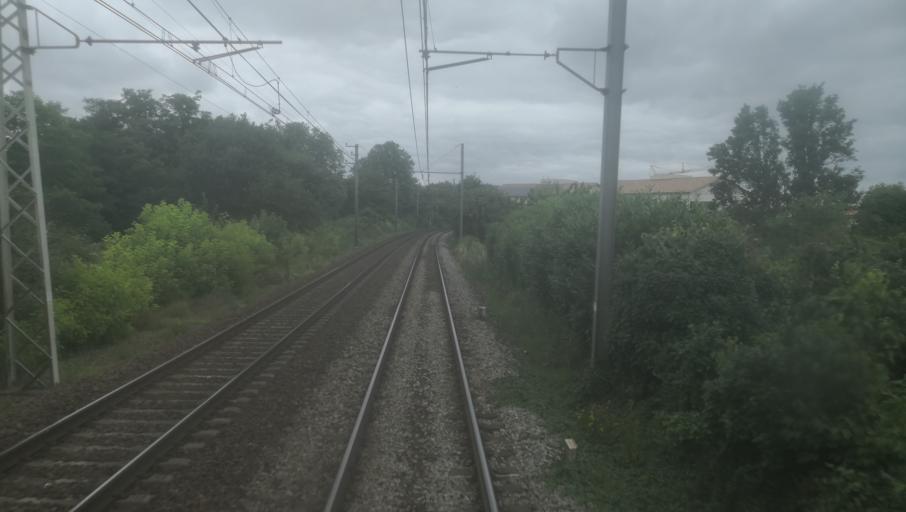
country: FR
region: Midi-Pyrenees
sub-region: Departement de la Haute-Garonne
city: Saint-Jory
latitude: 43.7412
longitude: 1.3686
